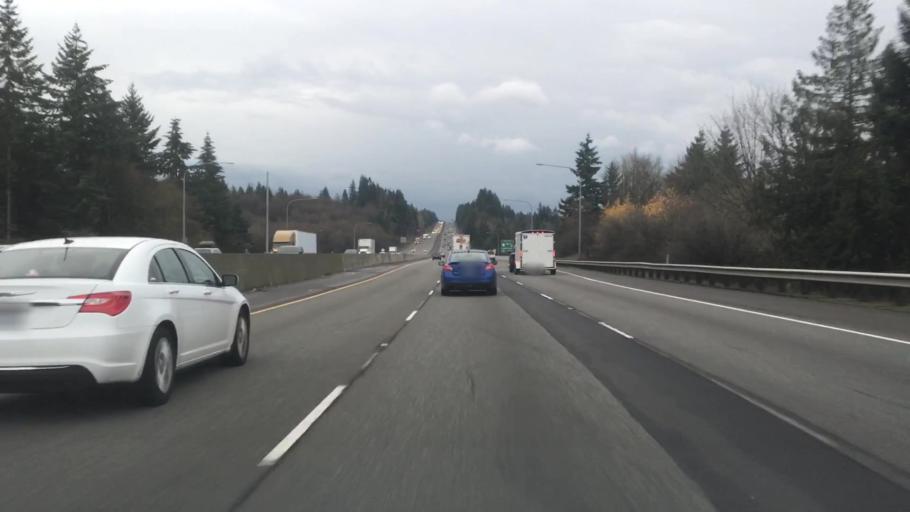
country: US
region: Washington
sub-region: Thurston County
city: Tenino
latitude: 46.8986
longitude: -122.9603
